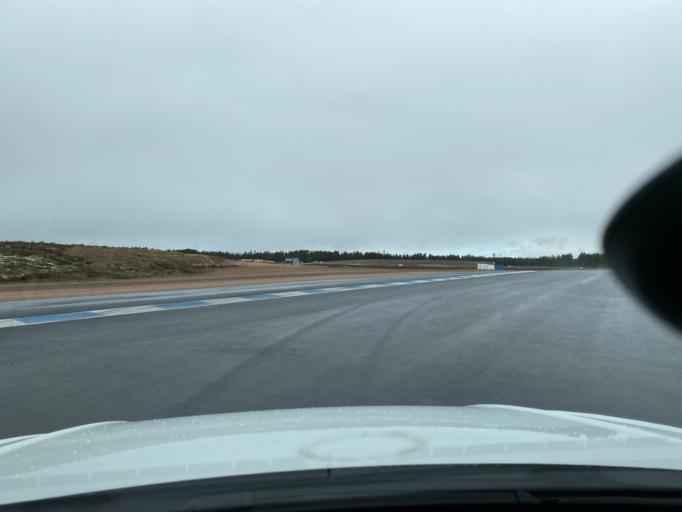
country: FI
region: Satakunta
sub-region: Pori
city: Vampula
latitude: 60.9760
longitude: 22.6705
